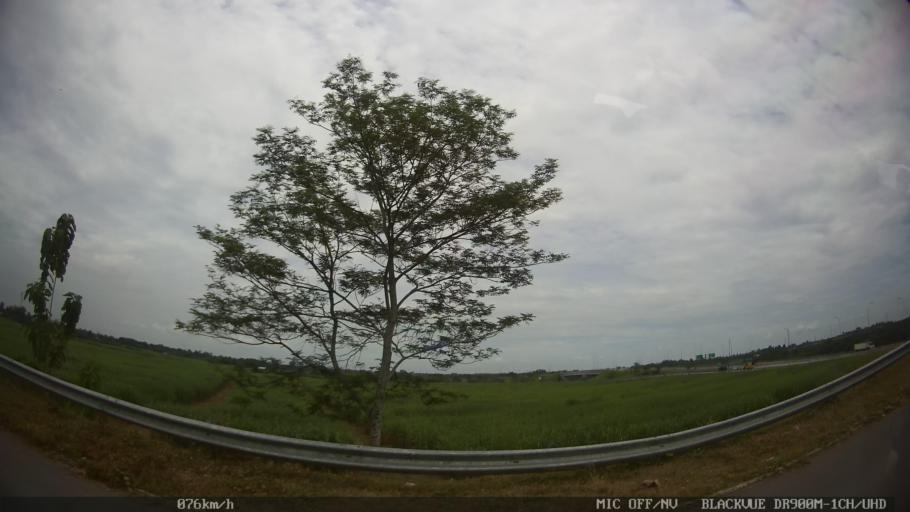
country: ID
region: North Sumatra
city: Sunggal
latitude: 3.6349
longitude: 98.5788
